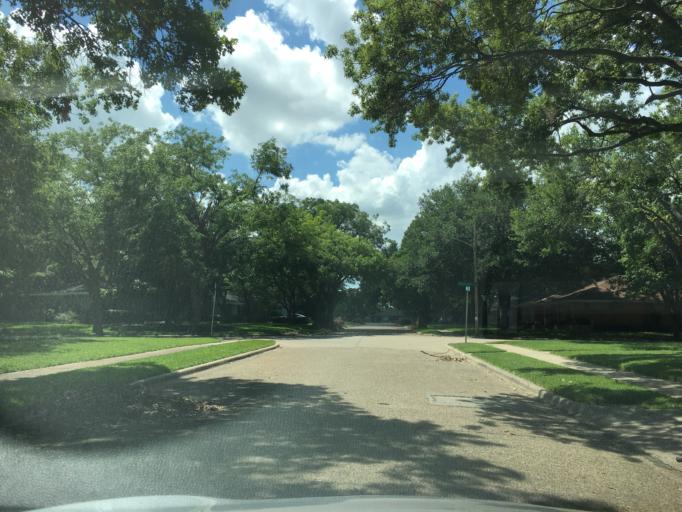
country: US
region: Texas
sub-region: Dallas County
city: Highland Park
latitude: 32.8522
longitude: -96.7569
